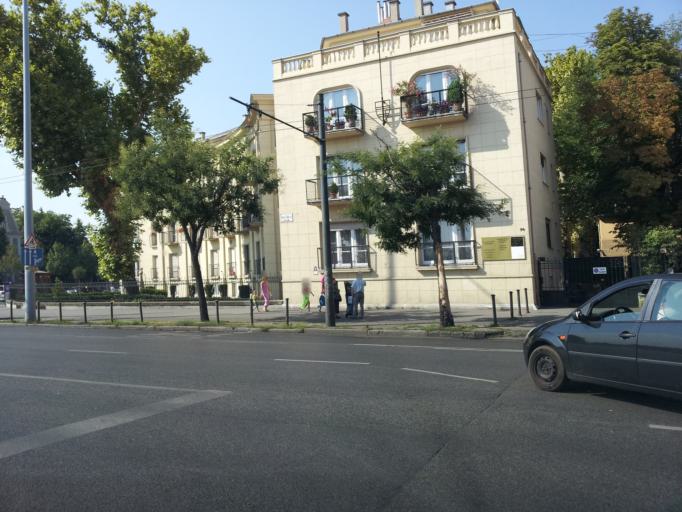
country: HU
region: Budapest
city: Budapest XIII. keruelet
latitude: 47.5150
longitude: 19.0766
